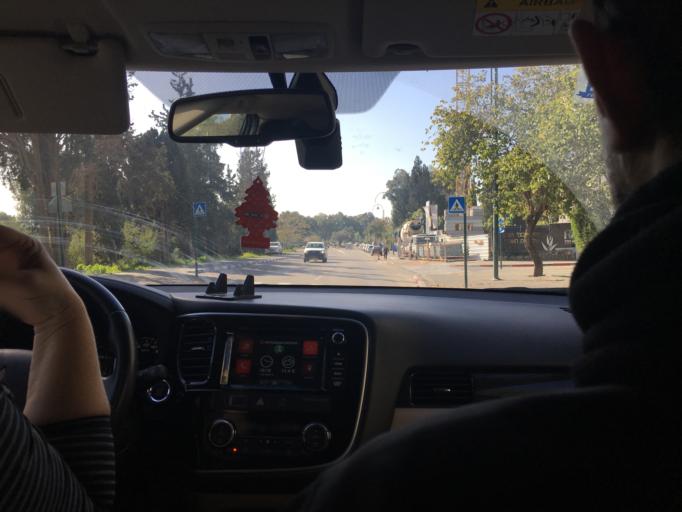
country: IL
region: Tel Aviv
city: Ramat HaSharon
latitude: 32.1426
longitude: 34.8468
